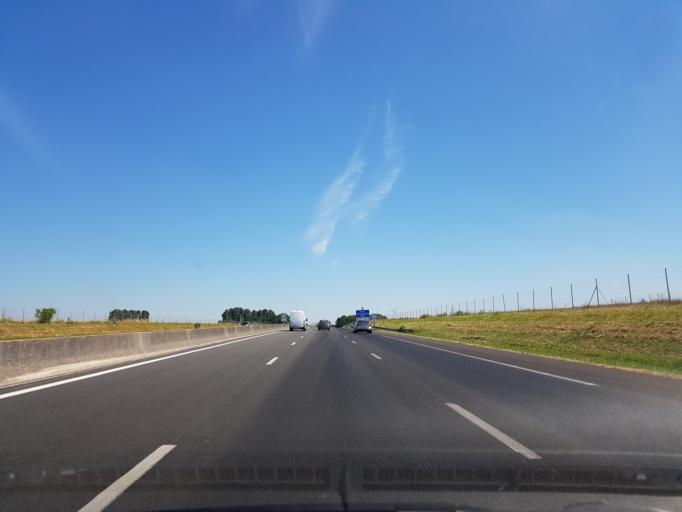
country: FR
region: Picardie
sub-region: Departement de la Somme
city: Roye
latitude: 49.7160
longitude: 2.7747
